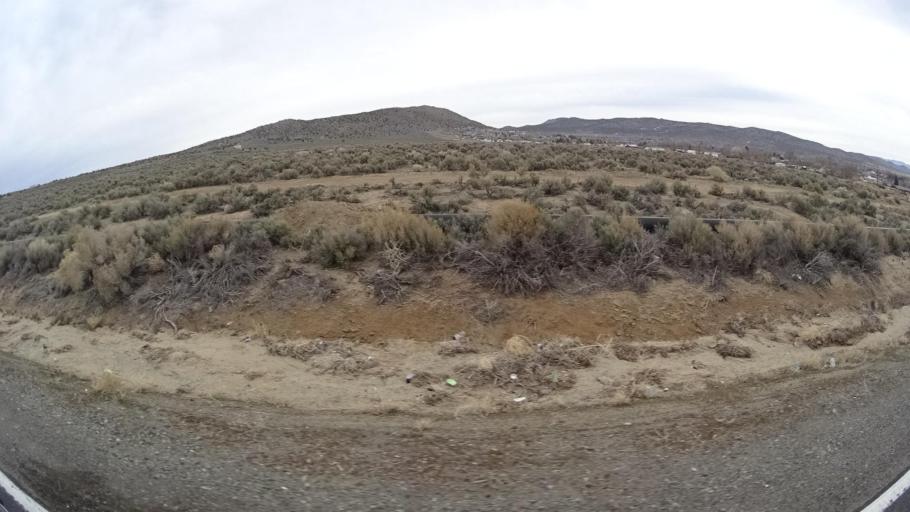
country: US
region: Nevada
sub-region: Washoe County
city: Lemmon Valley
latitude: 39.6757
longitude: -119.8506
